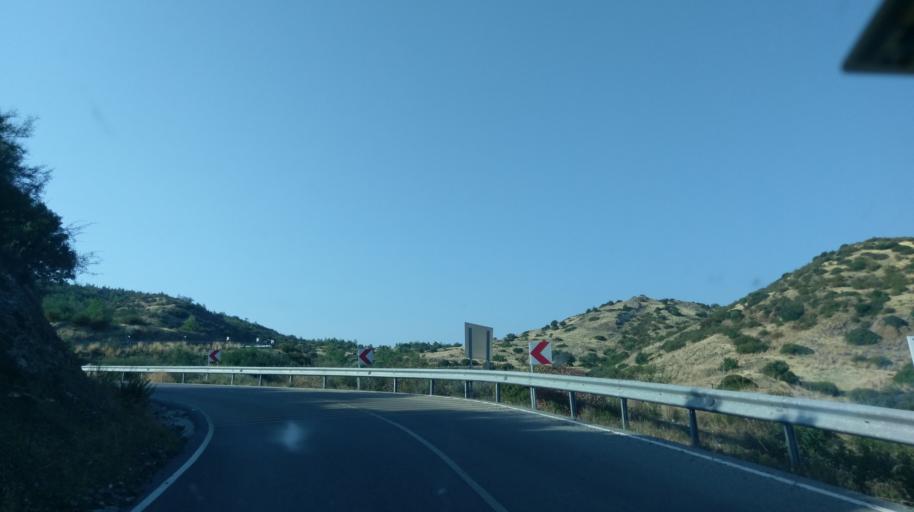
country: CY
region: Lefkosia
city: Kato Pyrgos
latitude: 35.1681
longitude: 32.7294
